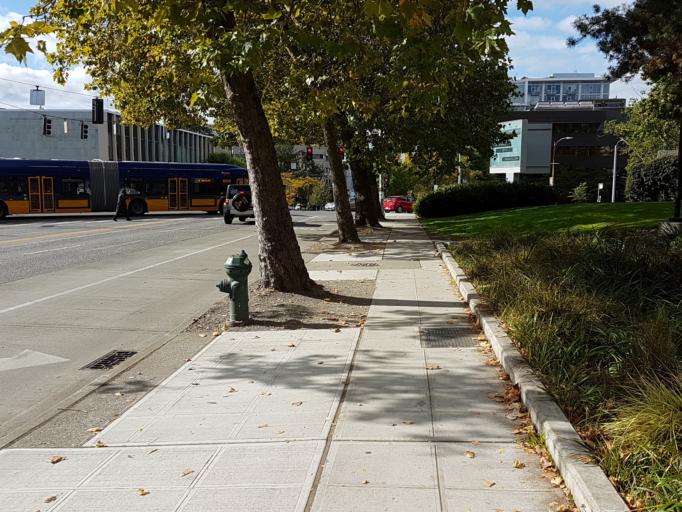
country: US
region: Washington
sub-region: King County
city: Seattle
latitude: 47.6190
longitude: -122.3499
